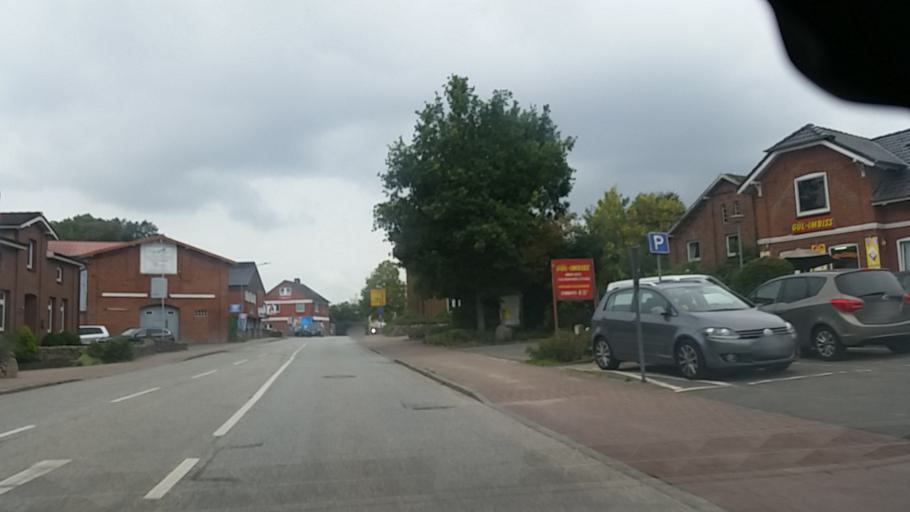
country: DE
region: Schleswig-Holstein
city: Leezen
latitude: 53.8677
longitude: 10.2524
